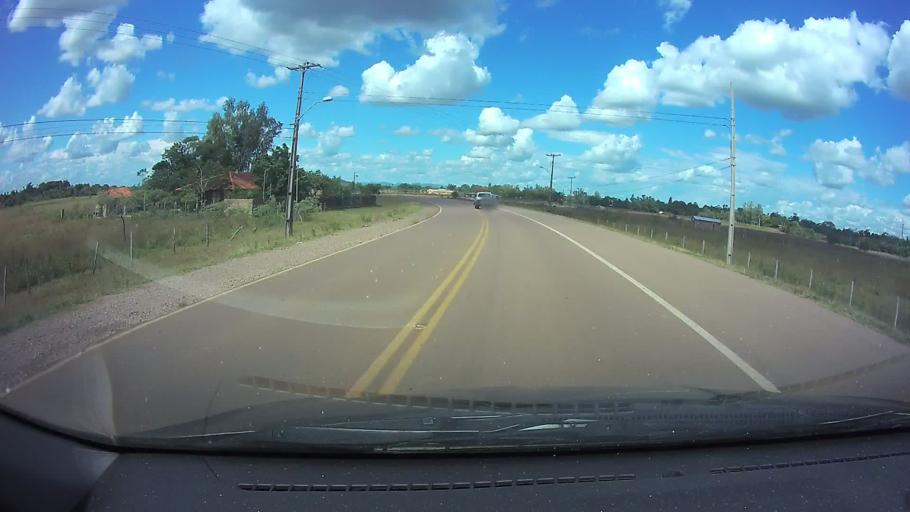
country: PY
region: Guaira
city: Itape
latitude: -25.9169
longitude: -56.6869
